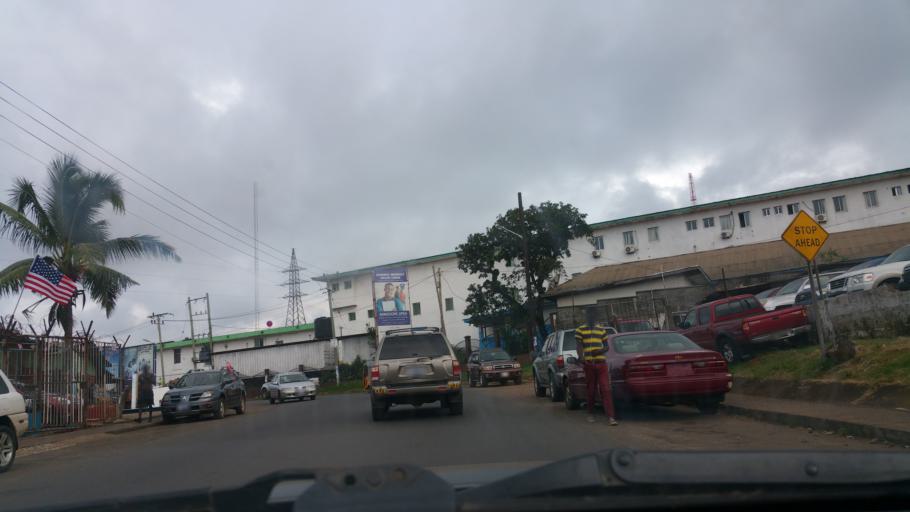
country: LR
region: Montserrado
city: Monrovia
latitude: 6.3057
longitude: -10.7959
